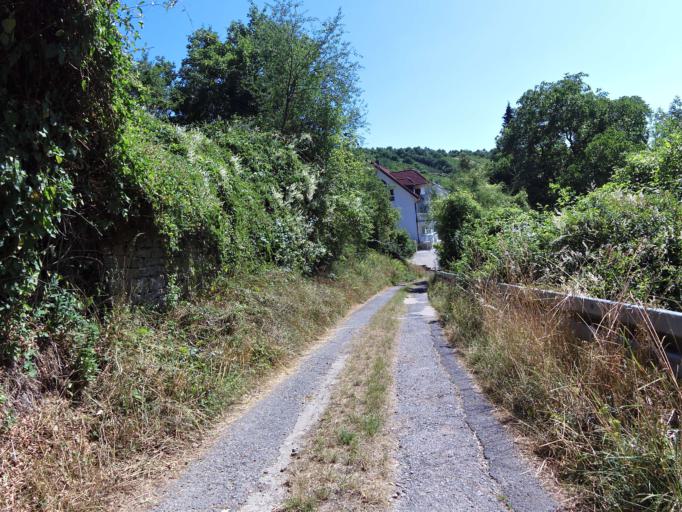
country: DE
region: Bavaria
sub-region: Regierungsbezirk Unterfranken
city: Randersacker
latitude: 49.7636
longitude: 9.9906
